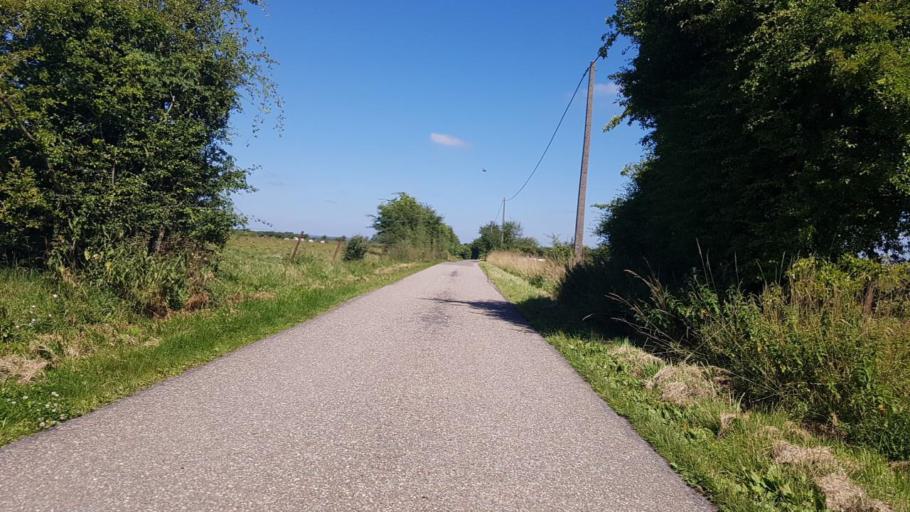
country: BE
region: Wallonia
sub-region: Province du Hainaut
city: Chimay
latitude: 50.0587
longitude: 4.2448
